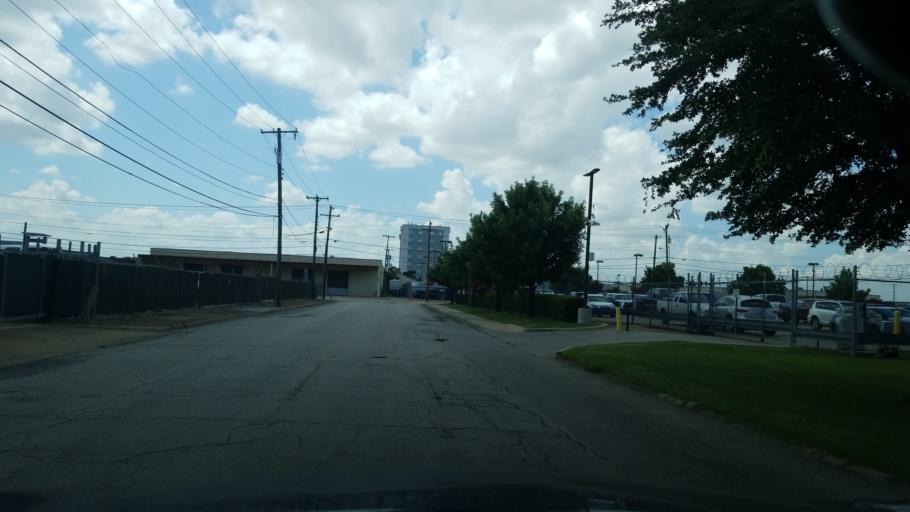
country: US
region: Texas
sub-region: Dallas County
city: University Park
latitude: 32.8317
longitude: -96.8334
